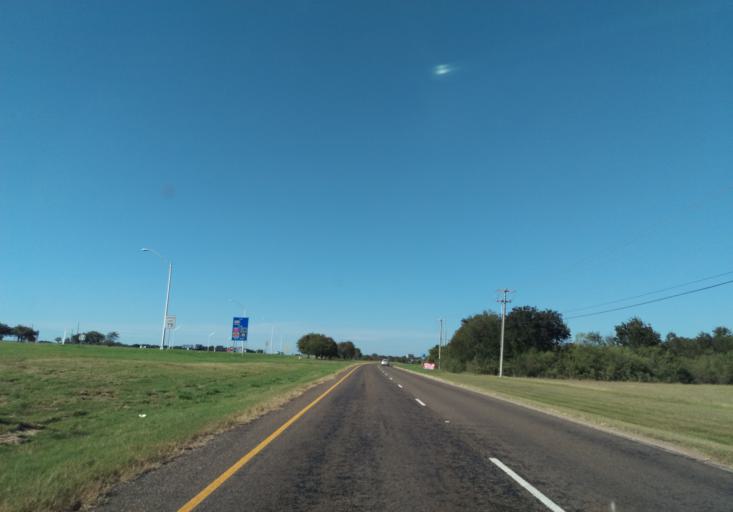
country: US
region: Texas
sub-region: Brazos County
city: College Station
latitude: 30.6260
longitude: -96.2994
